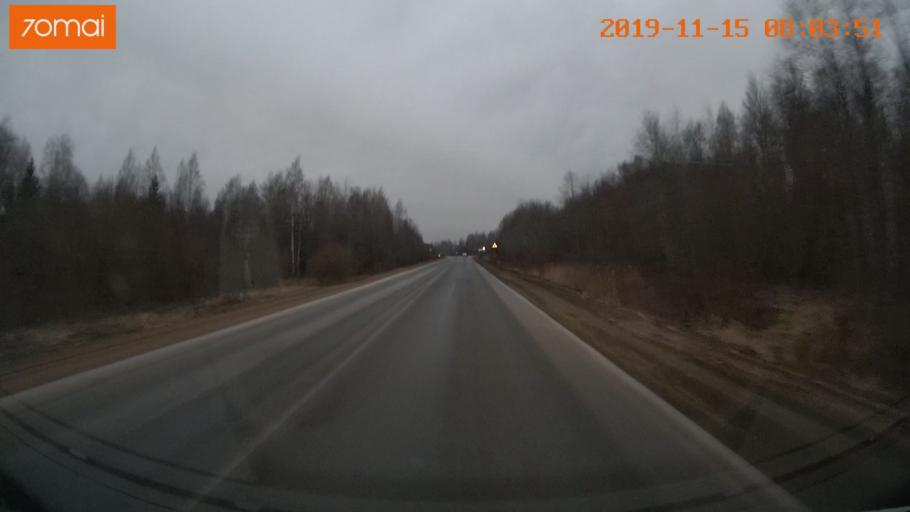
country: RU
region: Vologda
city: Cherepovets
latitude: 59.0023
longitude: 38.0839
